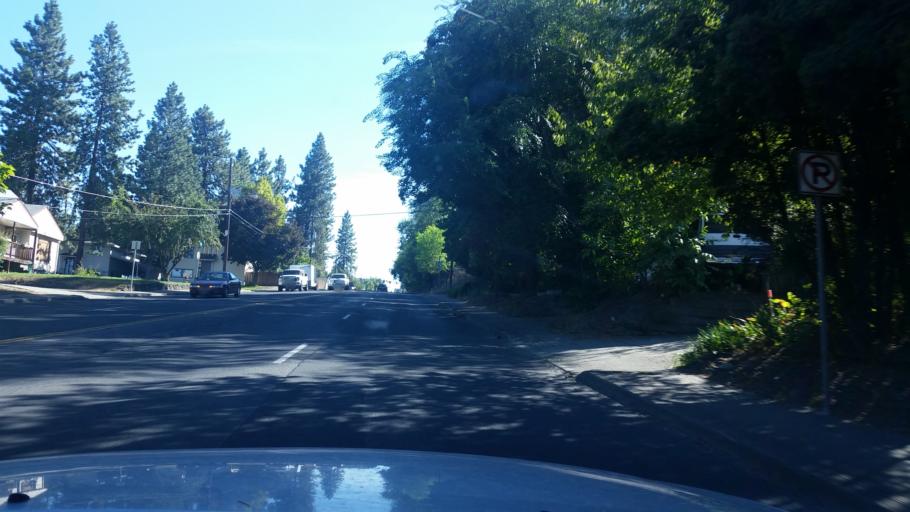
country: US
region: Washington
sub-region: Spokane County
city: Spokane
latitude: 47.6435
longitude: -117.3631
